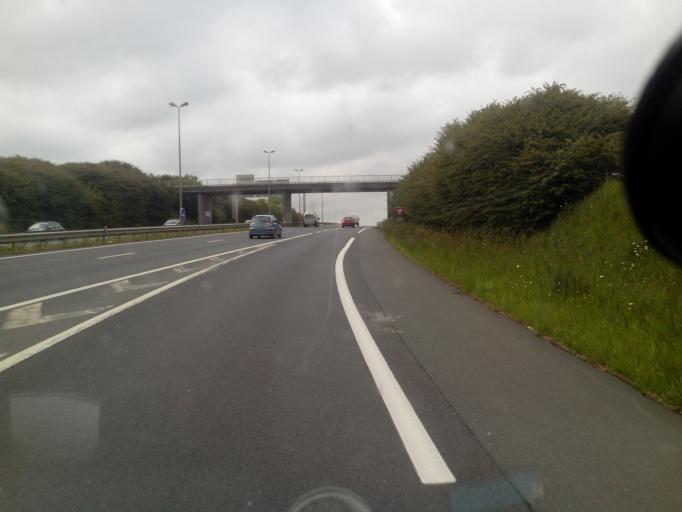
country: FR
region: Lower Normandy
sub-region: Departement du Calvados
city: Bretteville-sur-Odon
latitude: 49.1668
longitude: -0.4284
